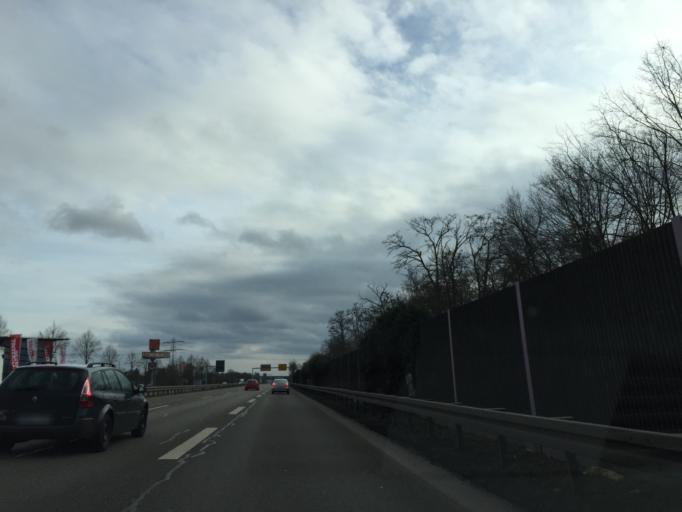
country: DE
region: Baden-Wuerttemberg
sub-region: Karlsruhe Region
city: Bruhl
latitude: 49.4157
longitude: 8.5410
